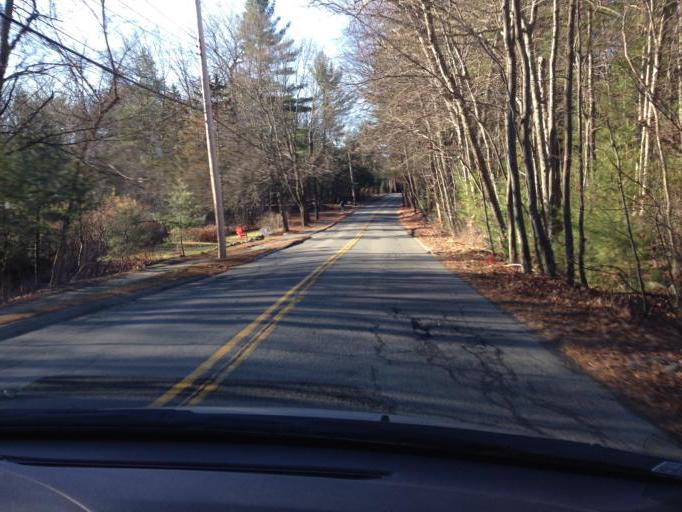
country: US
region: Massachusetts
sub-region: Middlesex County
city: Bedford
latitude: 42.5128
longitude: -71.2713
